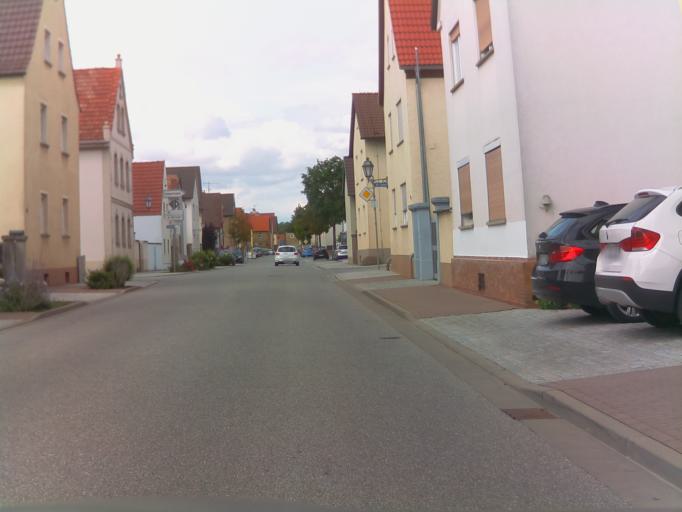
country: DE
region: Bavaria
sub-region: Regierungsbezirk Unterfranken
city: Grafenrheinfeld
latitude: 49.9988
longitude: 10.1980
